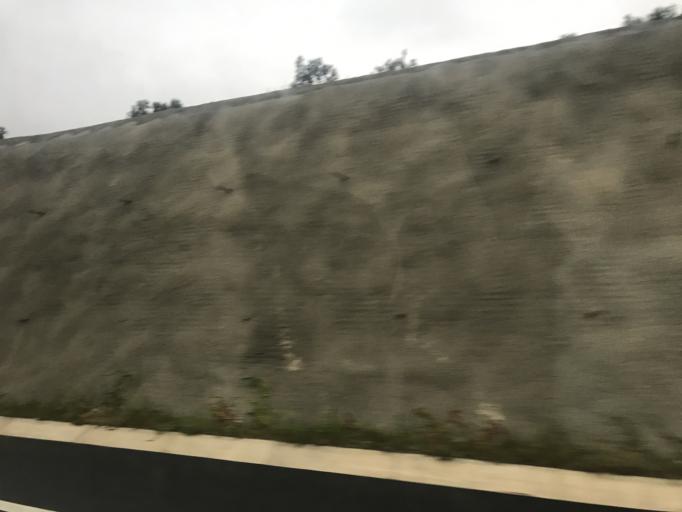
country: TR
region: Bursa
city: Umurbey
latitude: 40.4270
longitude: 29.2158
